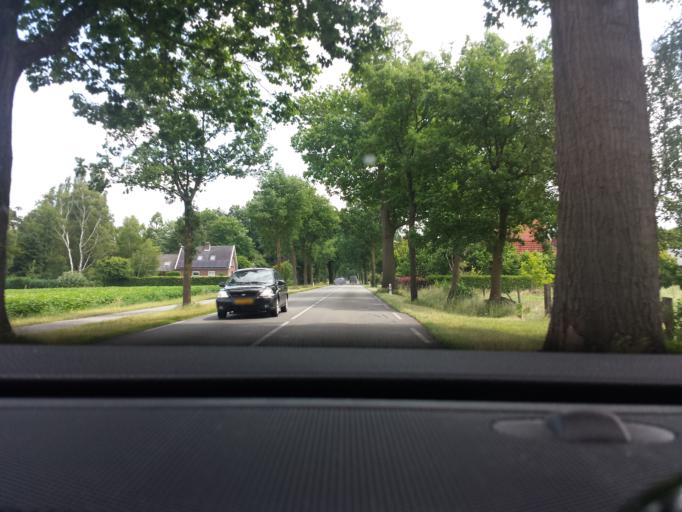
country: NL
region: Gelderland
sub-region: Berkelland
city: Neede
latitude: 52.1349
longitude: 6.6389
